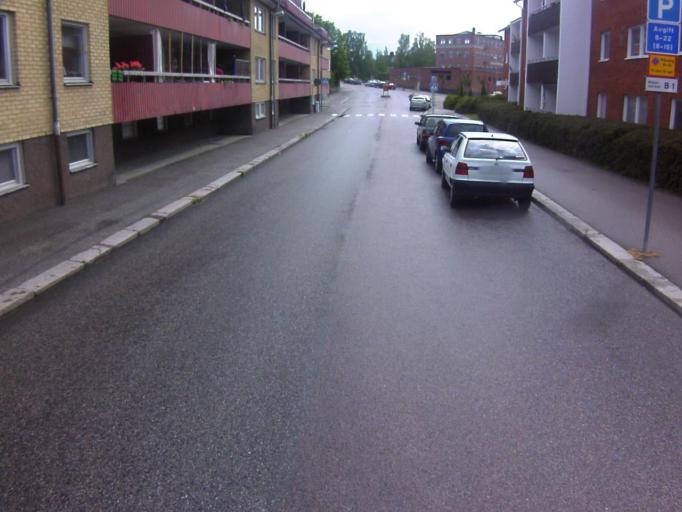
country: SE
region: Soedermanland
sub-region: Eskilstuna Kommun
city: Eskilstuna
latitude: 59.3641
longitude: 16.5173
